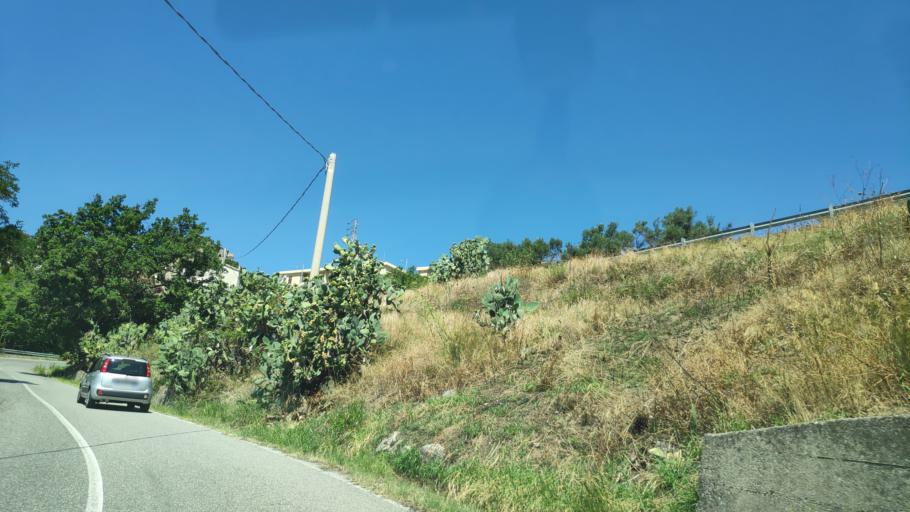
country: IT
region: Calabria
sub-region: Provincia di Catanzaro
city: Montauro
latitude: 38.7468
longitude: 16.5150
